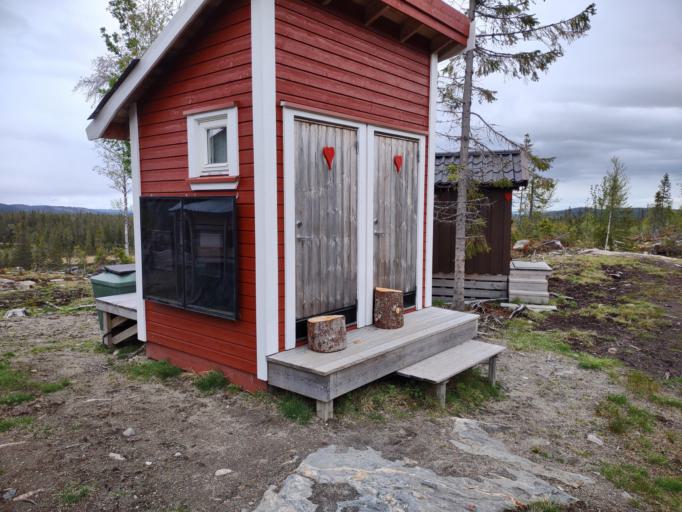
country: NO
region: Oppland
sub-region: Gran
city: Jaren
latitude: 60.4315
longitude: 10.6812
